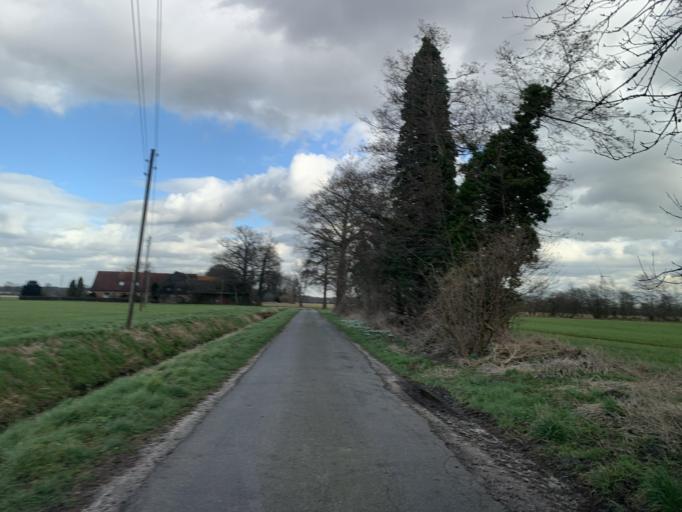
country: DE
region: North Rhine-Westphalia
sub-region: Regierungsbezirk Munster
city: Horstmar
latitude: 52.1088
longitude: 7.3111
